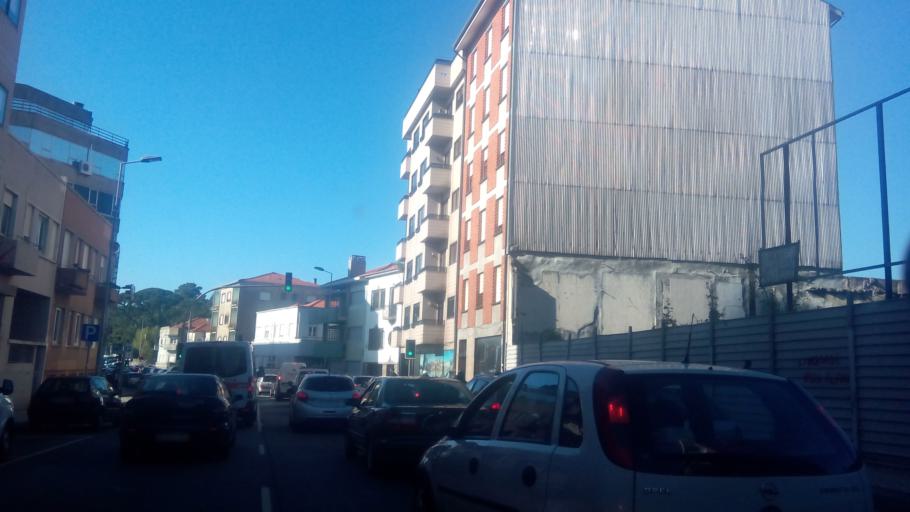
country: PT
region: Porto
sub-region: Porto
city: Porto
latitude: 41.1639
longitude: -8.6064
